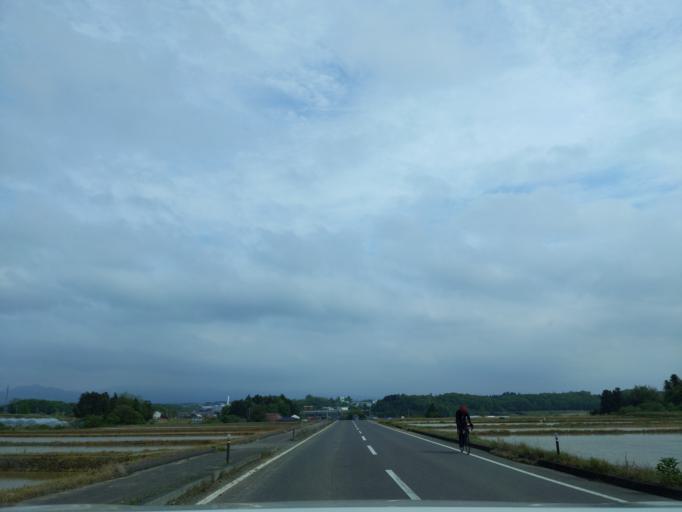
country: JP
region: Fukushima
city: Sukagawa
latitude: 37.3288
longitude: 140.3486
